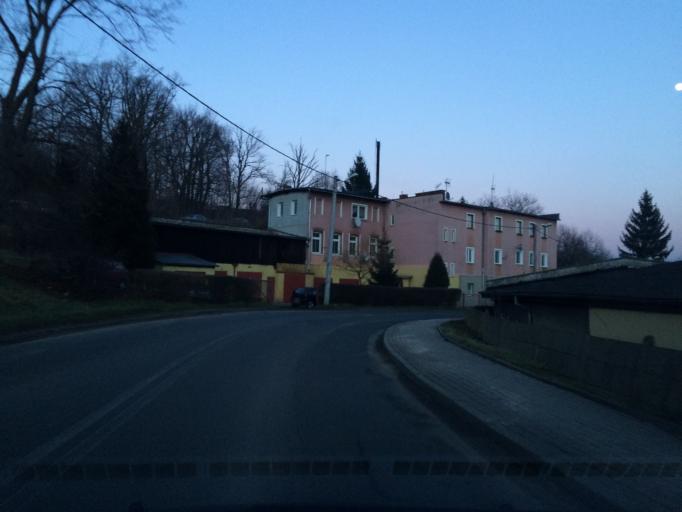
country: PL
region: Lower Silesian Voivodeship
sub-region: Powiat zlotoryjski
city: Zlotoryja
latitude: 51.1294
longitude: 15.9112
